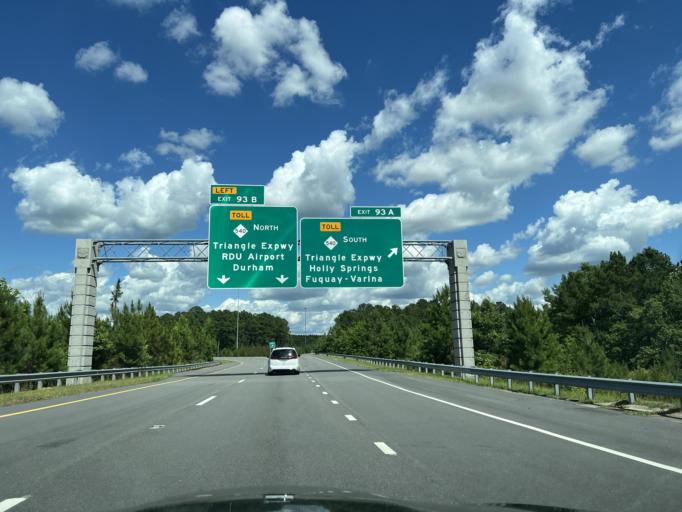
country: US
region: North Carolina
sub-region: Wake County
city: Apex
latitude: 35.6947
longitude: -78.8748
